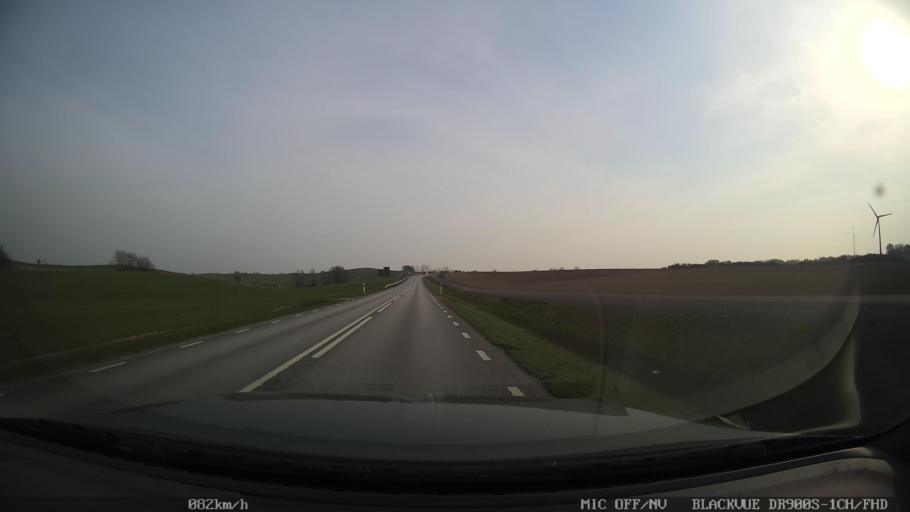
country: SE
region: Skane
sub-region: Ystads Kommun
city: Ystad
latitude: 55.4670
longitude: 13.7976
